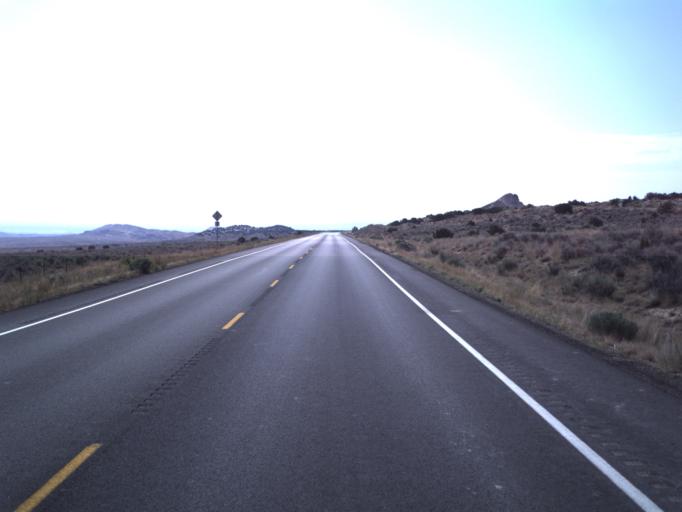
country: US
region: Utah
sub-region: Uintah County
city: Naples
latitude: 40.3546
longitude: -109.4959
